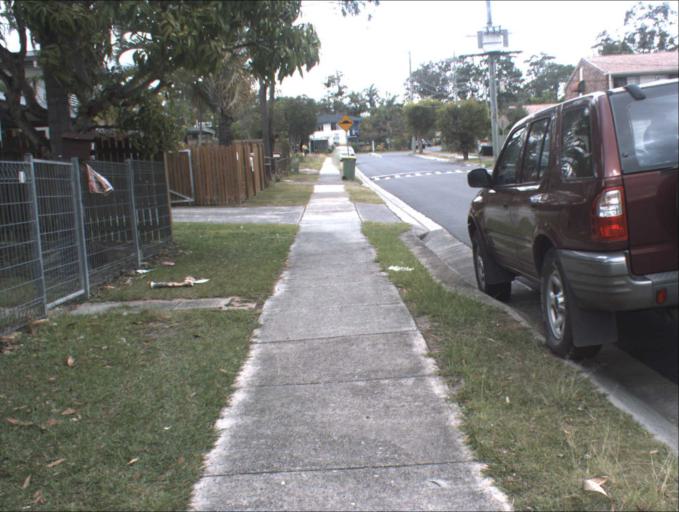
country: AU
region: Queensland
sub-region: Logan
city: Logan City
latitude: -27.6450
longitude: 153.1145
